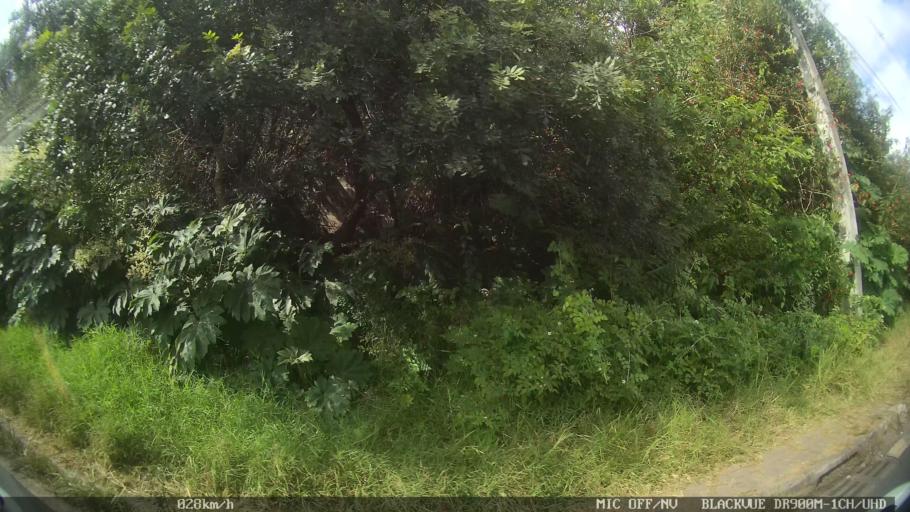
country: BR
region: Parana
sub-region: Pinhais
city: Pinhais
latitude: -25.3831
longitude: -49.2039
